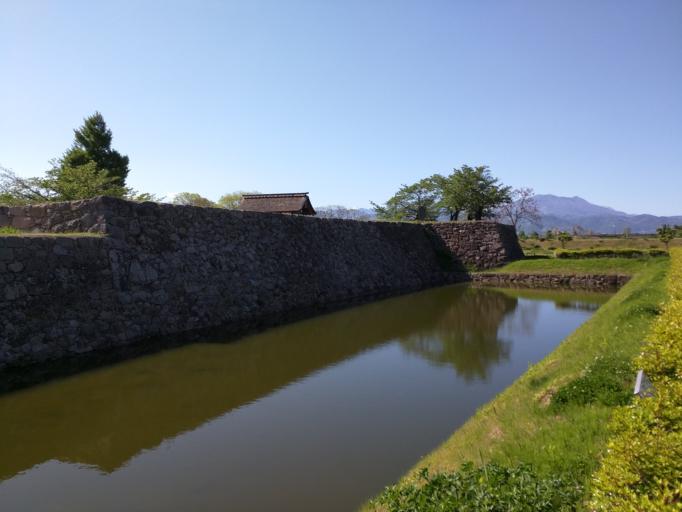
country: JP
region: Nagano
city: Nagano-shi
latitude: 36.5659
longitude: 138.1967
